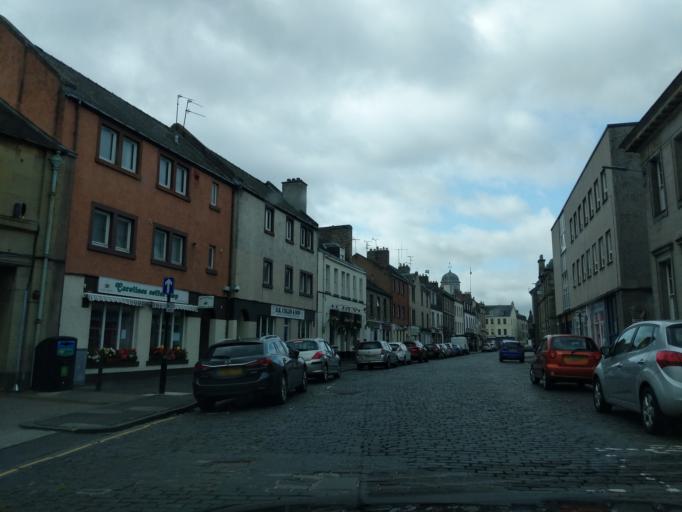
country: GB
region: Scotland
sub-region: The Scottish Borders
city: Kelso
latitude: 55.5995
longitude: -2.4318
